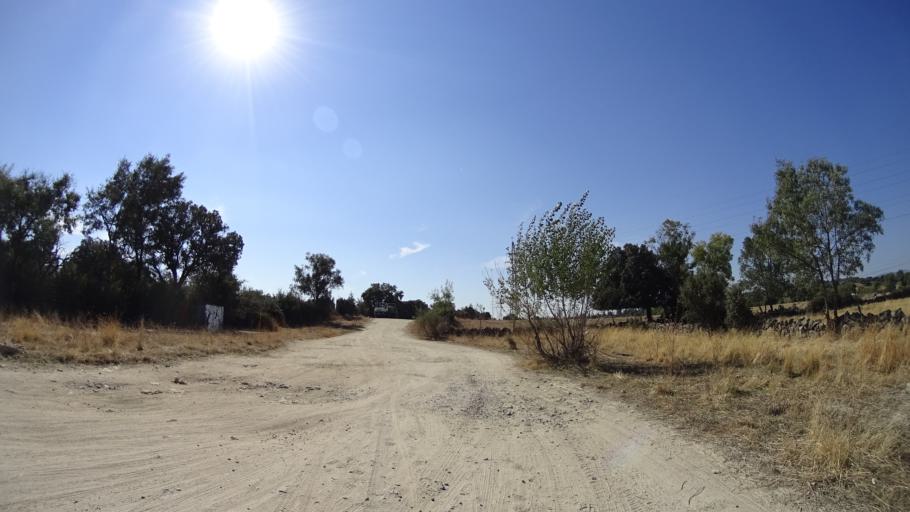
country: ES
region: Madrid
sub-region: Provincia de Madrid
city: Collado-Villalba
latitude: 40.6134
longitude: -4.0206
